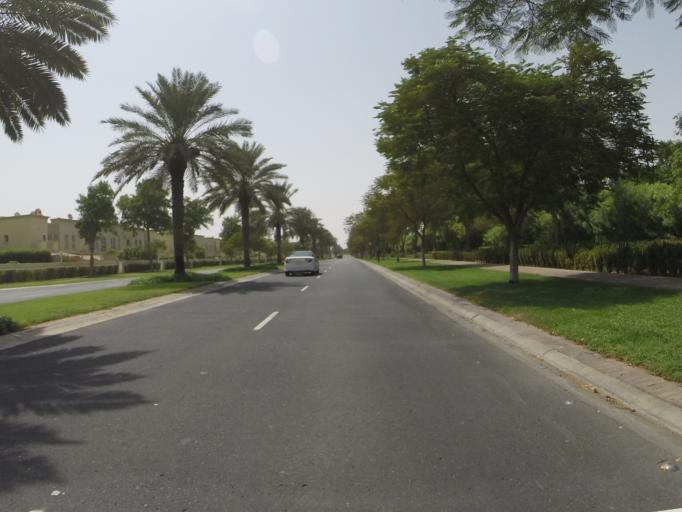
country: AE
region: Dubai
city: Dubai
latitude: 25.0601
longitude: 55.1602
